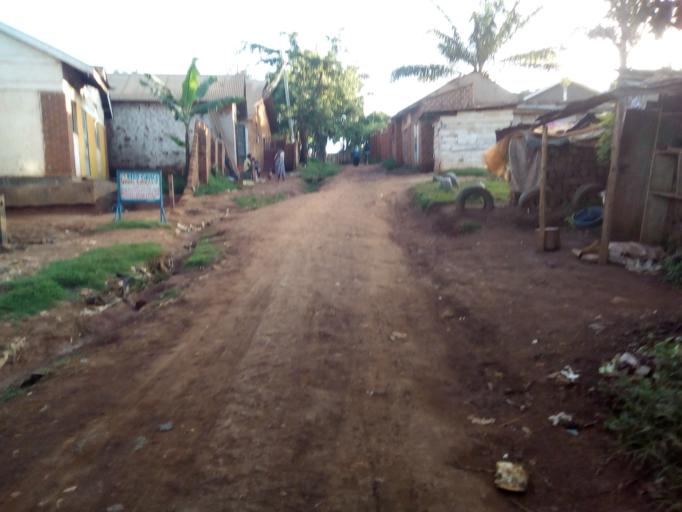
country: UG
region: Central Region
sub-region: Wakiso District
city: Kajansi
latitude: 0.2482
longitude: 32.5758
